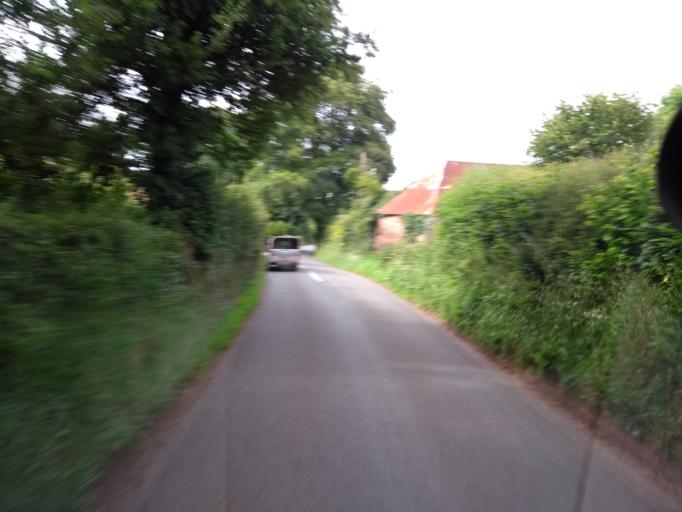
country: GB
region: England
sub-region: Somerset
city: Wiveliscombe
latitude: 51.1002
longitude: -3.3042
